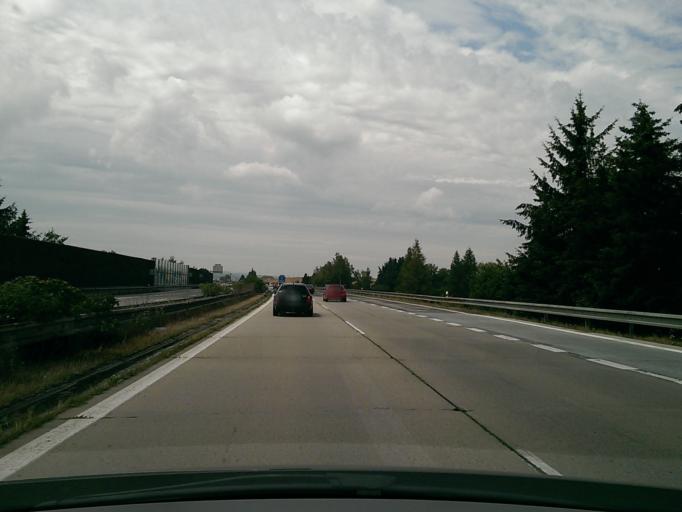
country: CZ
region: Vysocina
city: Merin
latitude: 49.3969
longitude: 15.8852
